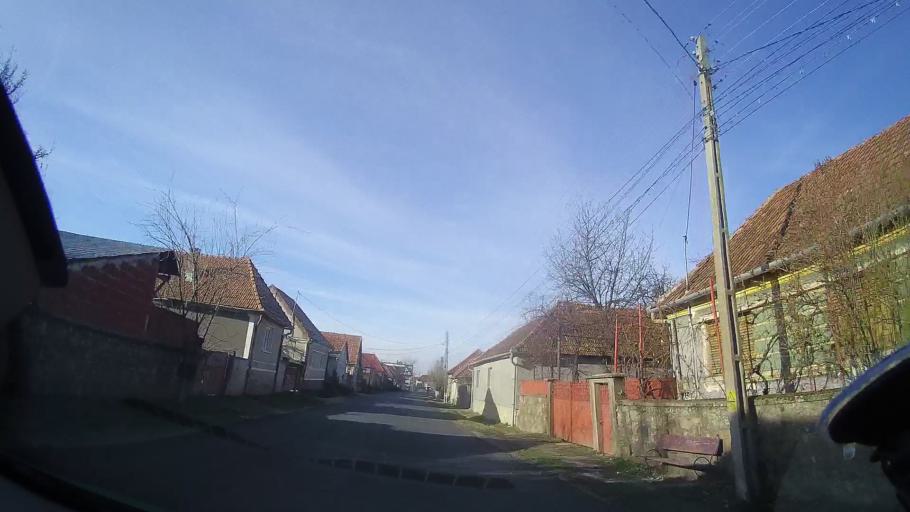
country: RO
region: Bihor
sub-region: Comuna Magesti
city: Magesti
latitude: 47.0160
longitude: 22.4354
